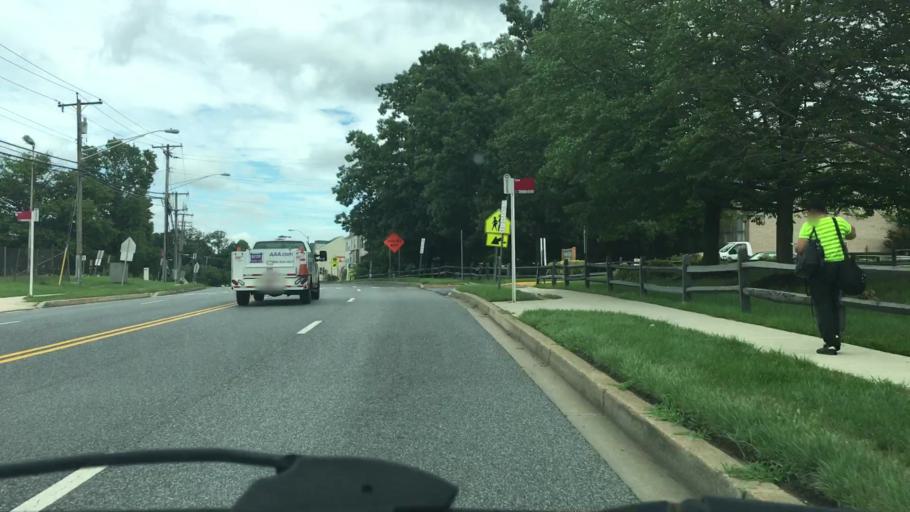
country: US
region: Maryland
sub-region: Prince George's County
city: Goddard
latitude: 38.9875
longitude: -76.8373
